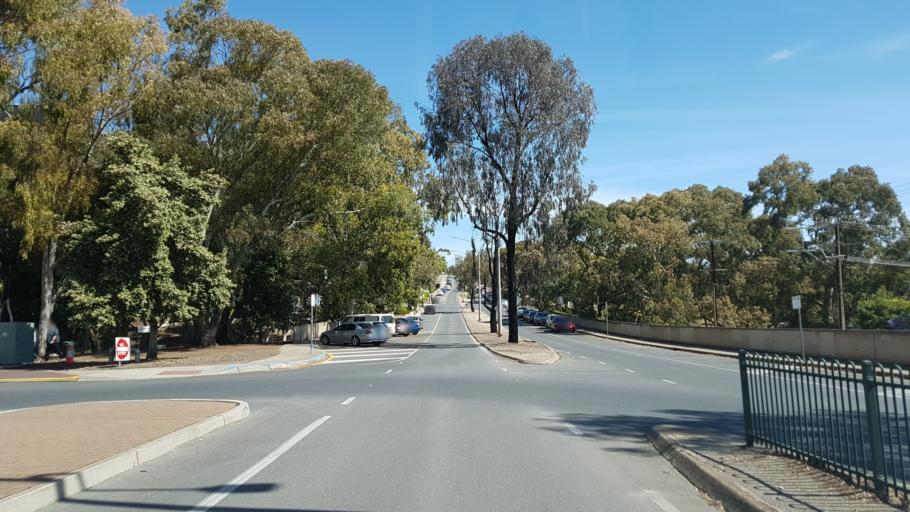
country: AU
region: South Australia
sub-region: Marion
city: Marion
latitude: -35.0219
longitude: 138.5677
